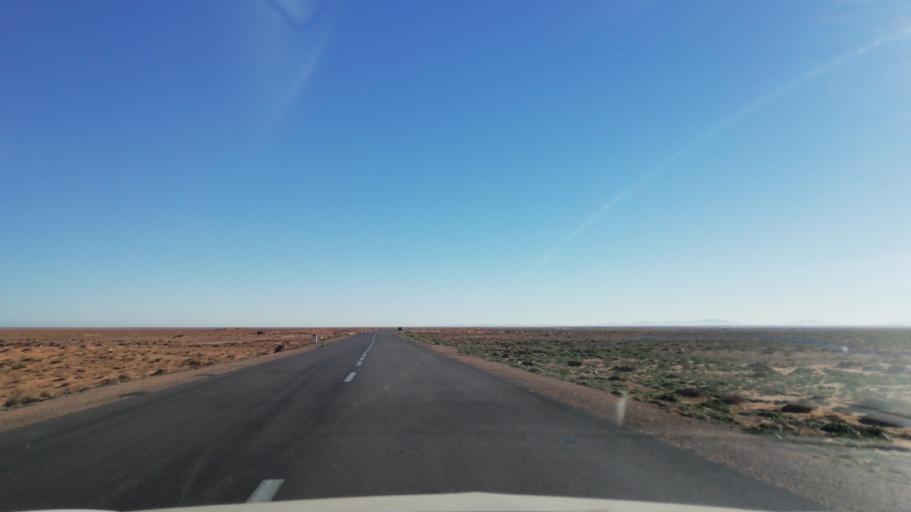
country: DZ
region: El Bayadh
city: El Bayadh
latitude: 33.8598
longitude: 0.5503
